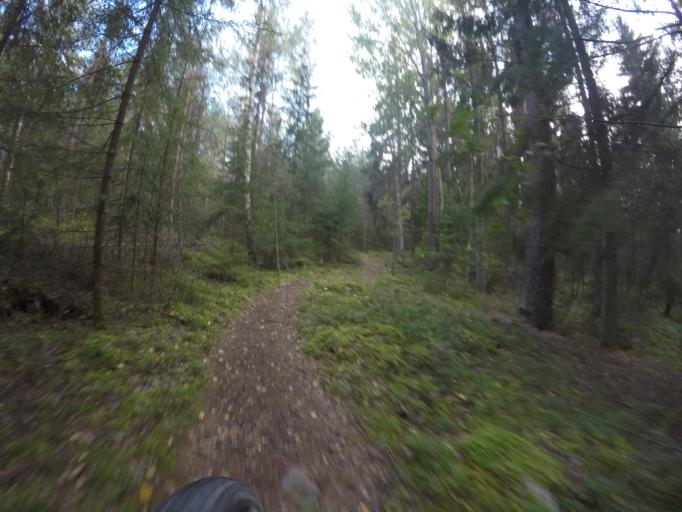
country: SE
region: Vaestmanland
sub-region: Kopings Kommun
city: Koping
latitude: 59.5359
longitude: 15.9972
